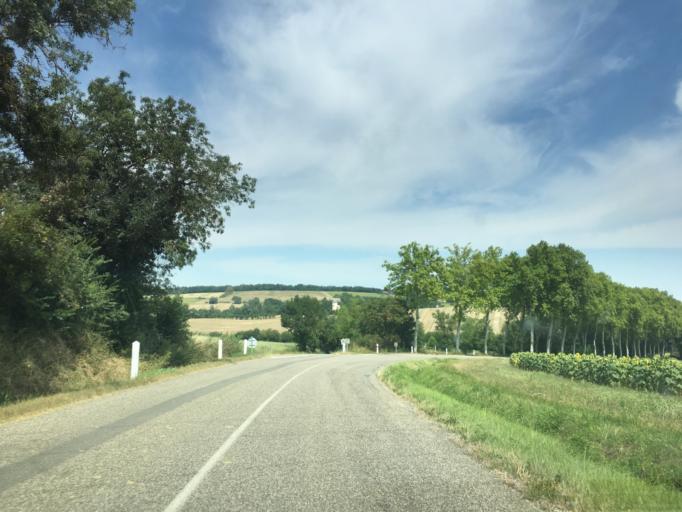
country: FR
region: Midi-Pyrenees
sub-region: Departement du Gers
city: Fleurance
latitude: 43.8603
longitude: 0.6835
